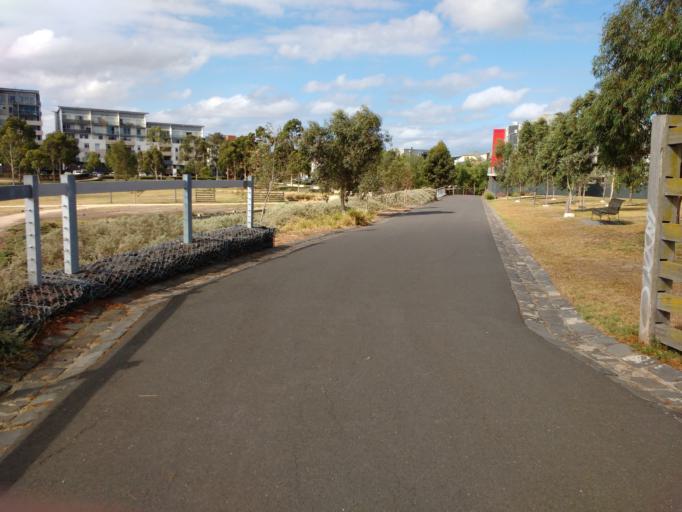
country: AU
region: Victoria
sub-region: Melbourne
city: Ascot Vale
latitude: -37.7958
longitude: 144.9157
